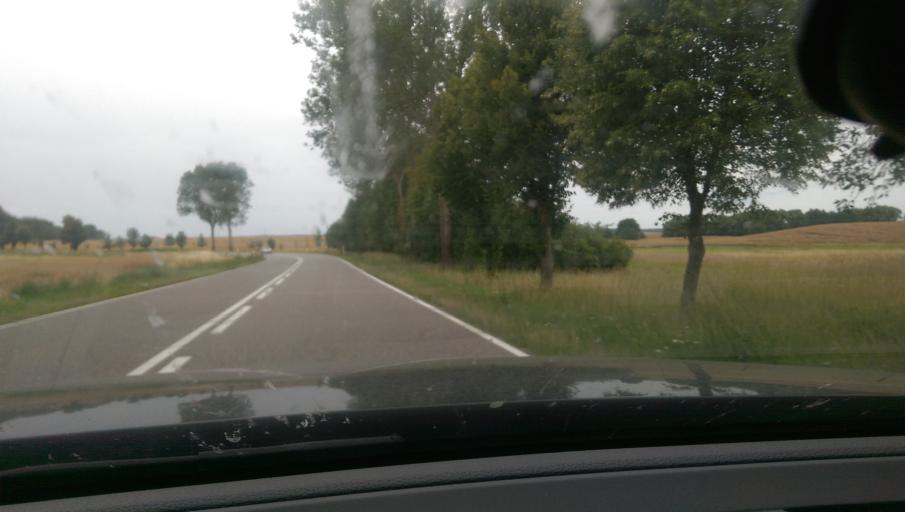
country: PL
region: Warmian-Masurian Voivodeship
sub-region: Powiat elcki
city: Elk
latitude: 53.8578
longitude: 22.5014
